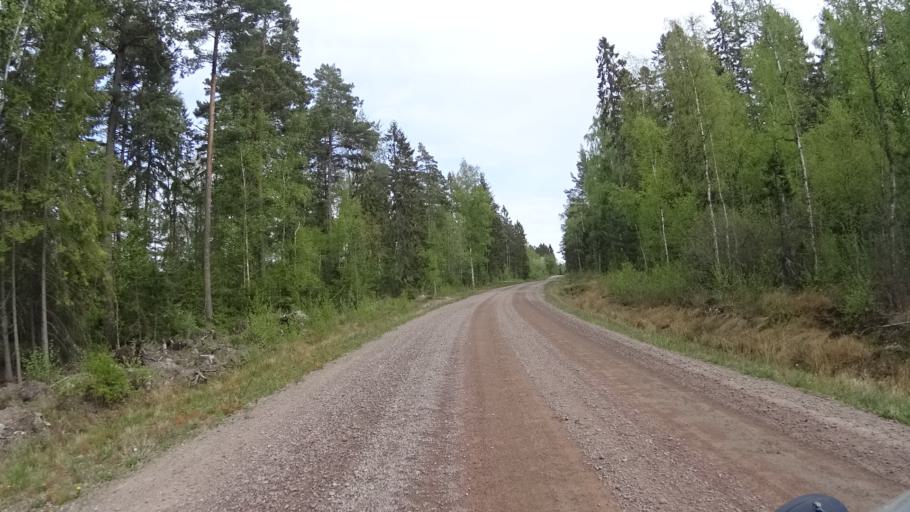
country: SE
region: Vaestra Goetaland
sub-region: Karlsborgs Kommun
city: Karlsborg
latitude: 58.5008
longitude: 14.4697
